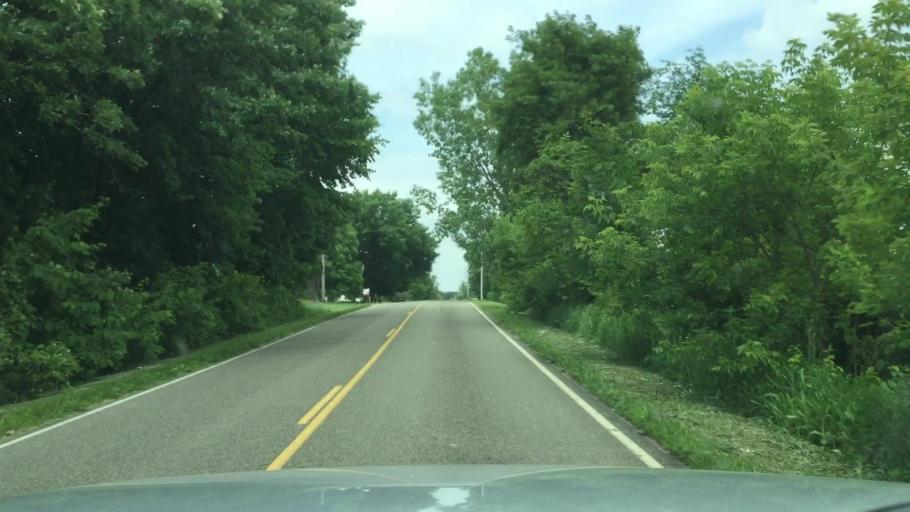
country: US
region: Michigan
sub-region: Shiawassee County
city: Durand
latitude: 42.9444
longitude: -83.9591
